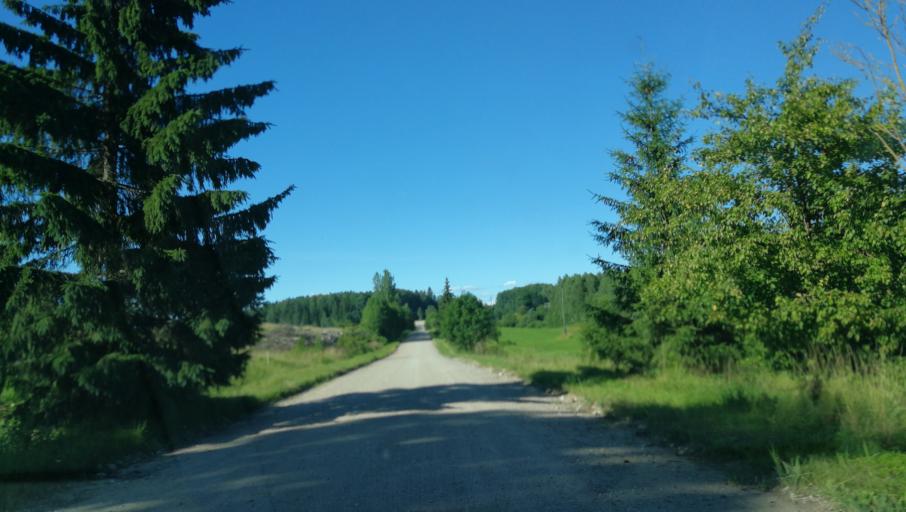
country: LV
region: Jaunpiebalga
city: Jaunpiebalga
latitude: 57.0009
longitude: 26.0301
